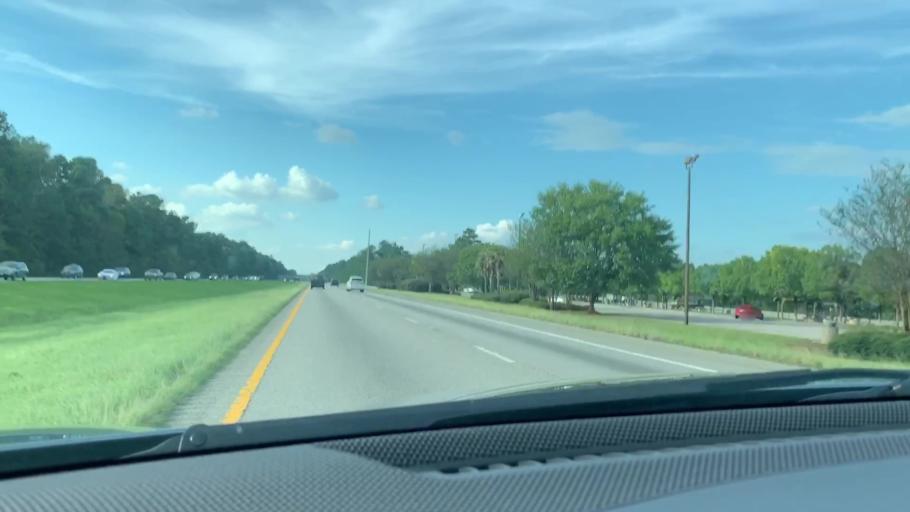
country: US
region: South Carolina
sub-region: Orangeburg County
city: Brookdale
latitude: 33.4791
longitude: -80.7552
